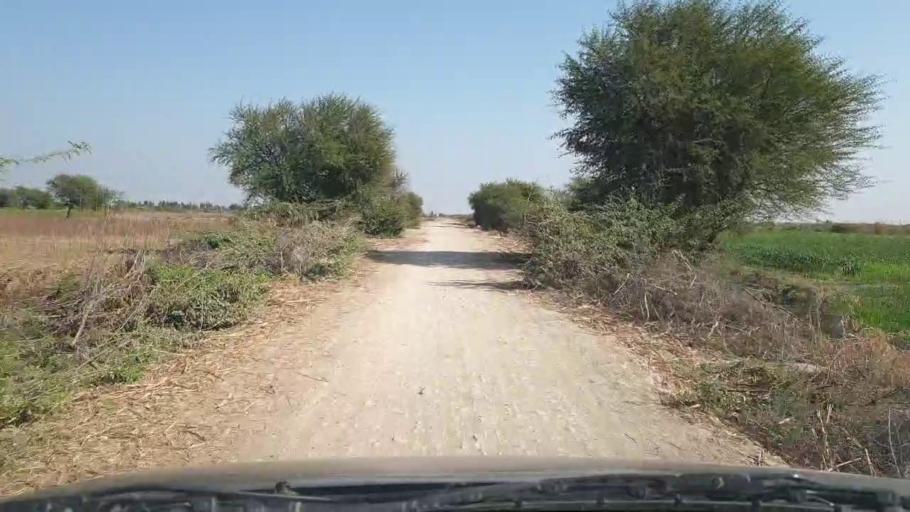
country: PK
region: Sindh
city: Samaro
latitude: 25.1971
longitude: 69.2726
